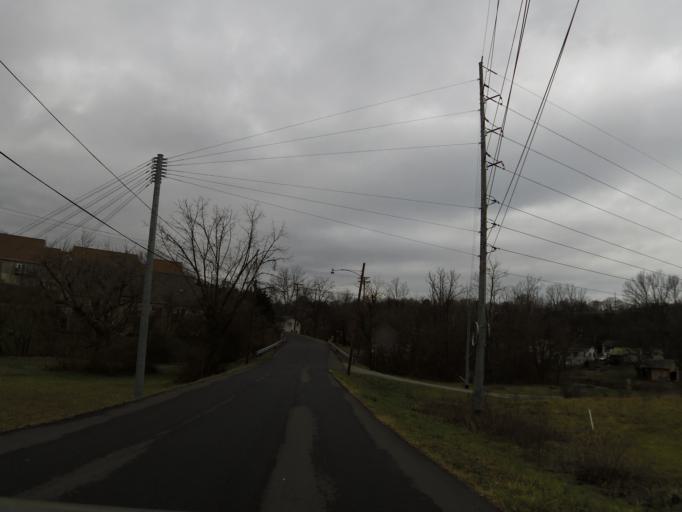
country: US
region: Tennessee
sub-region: Jefferson County
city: Jefferson City
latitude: 36.1280
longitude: -83.4858
